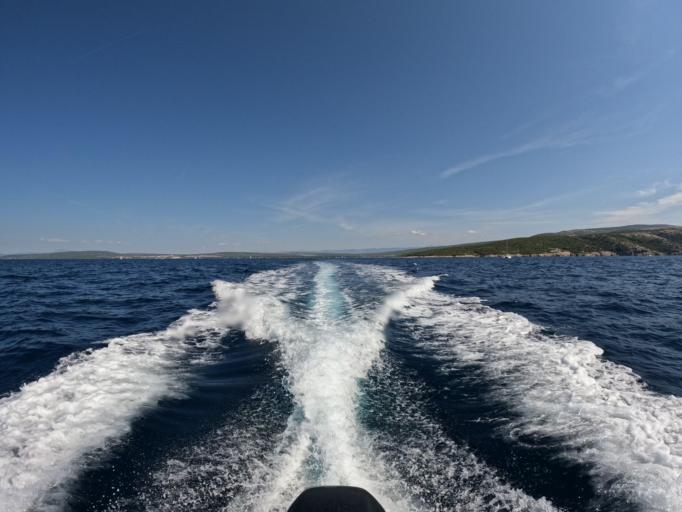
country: HR
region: Primorsko-Goranska
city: Punat
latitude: 44.9694
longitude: 14.6085
